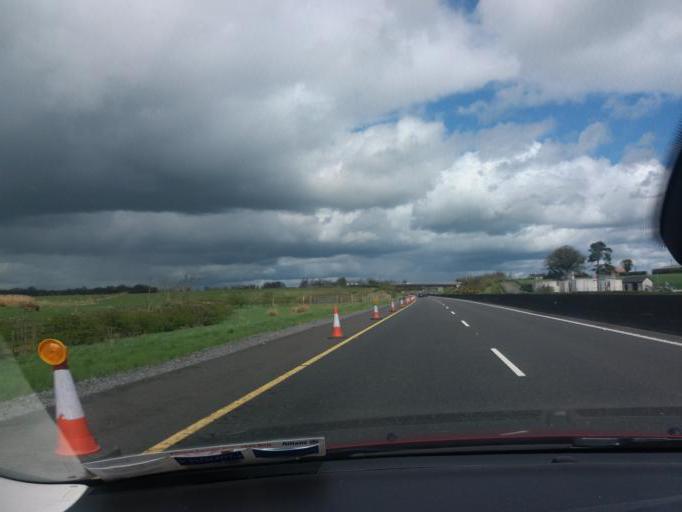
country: IE
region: Leinster
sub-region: Laois
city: Rathdowney
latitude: 52.7473
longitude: -7.5745
